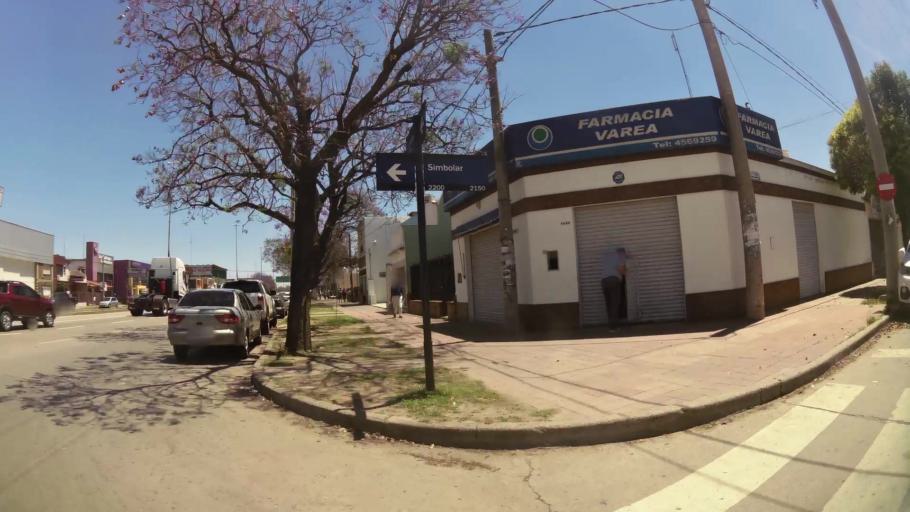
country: AR
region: Cordoba
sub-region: Departamento de Capital
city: Cordoba
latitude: -31.4369
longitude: -64.1291
